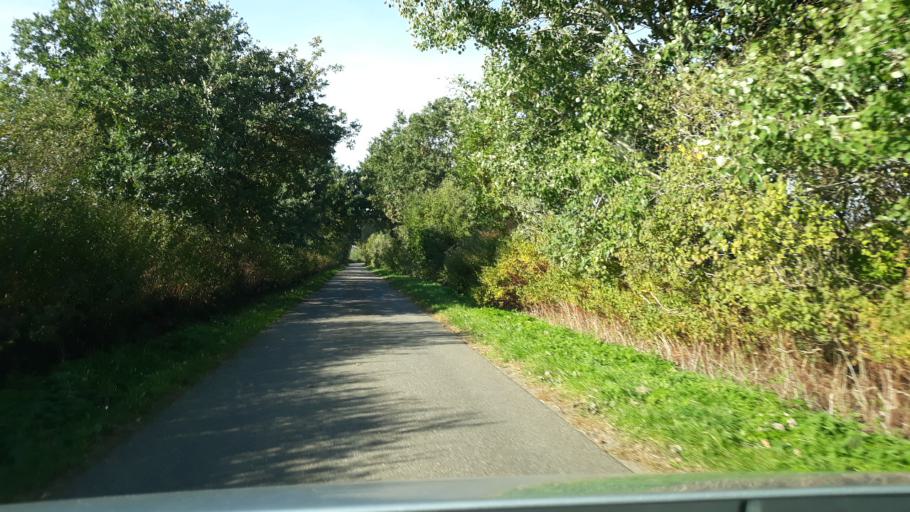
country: DE
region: Schleswig-Holstein
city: Borm
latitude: 54.4228
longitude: 9.4071
